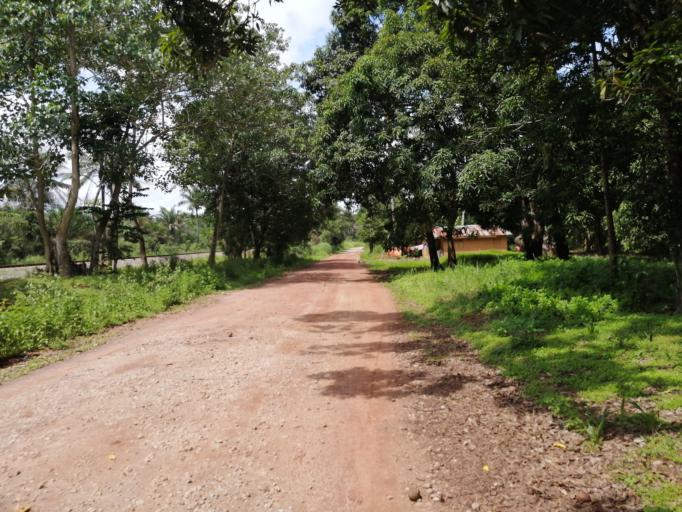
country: SL
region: Northern Province
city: Pepel
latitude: 8.6819
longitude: -12.9995
